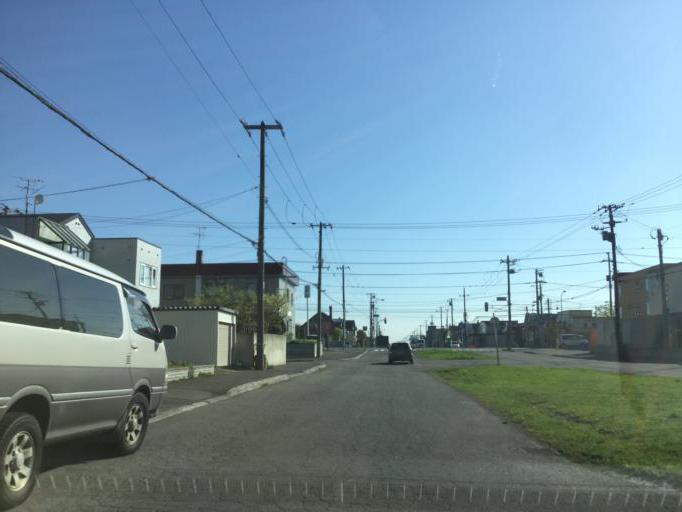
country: JP
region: Hokkaido
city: Ebetsu
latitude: 43.0826
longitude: 141.5322
